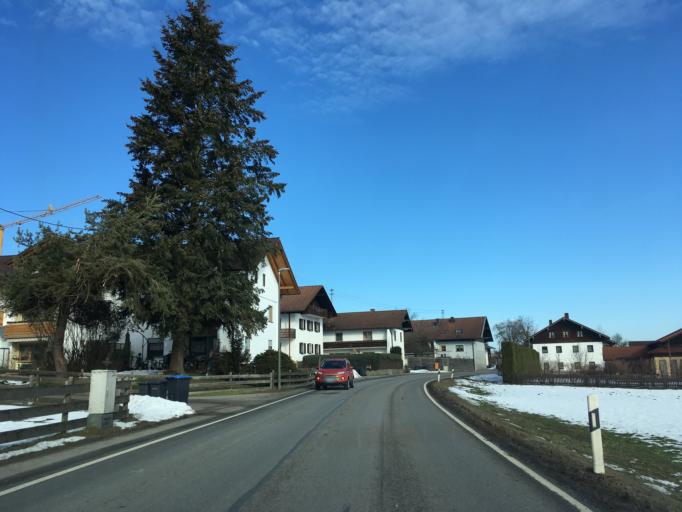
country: DE
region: Bavaria
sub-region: Upper Bavaria
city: Schechen
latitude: 47.8966
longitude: 12.1544
